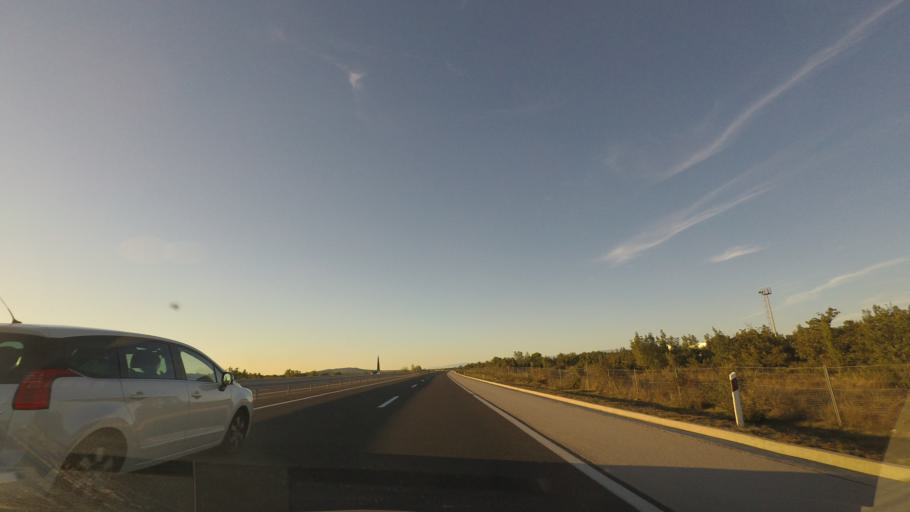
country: HR
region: Zadarska
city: Benkovac
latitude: 44.0244
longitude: 15.5701
